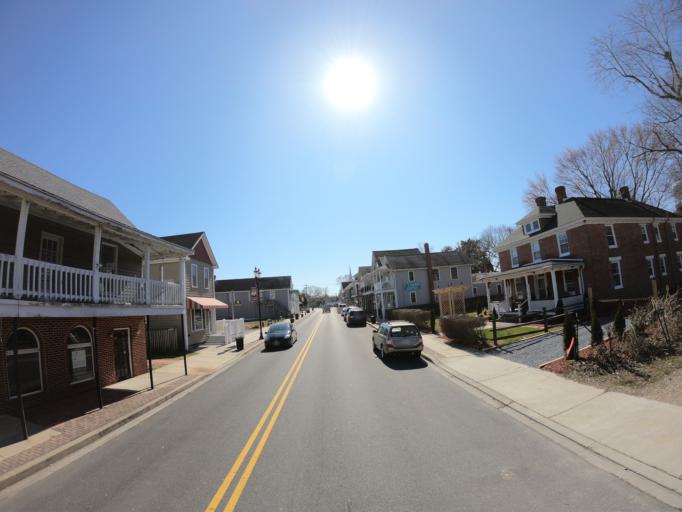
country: US
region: Maryland
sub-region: Kent County
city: Rock Hall
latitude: 39.1377
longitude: -76.2348
